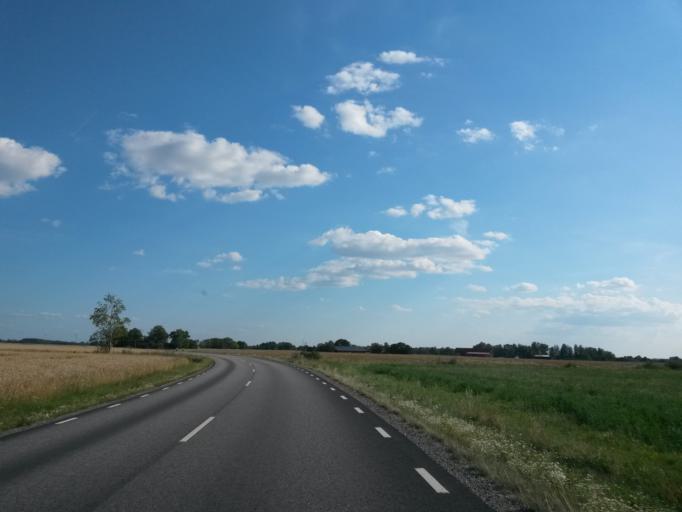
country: SE
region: Vaestra Goetaland
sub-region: Lidkopings Kommun
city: Lidkoping
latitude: 58.4117
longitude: 13.1627
